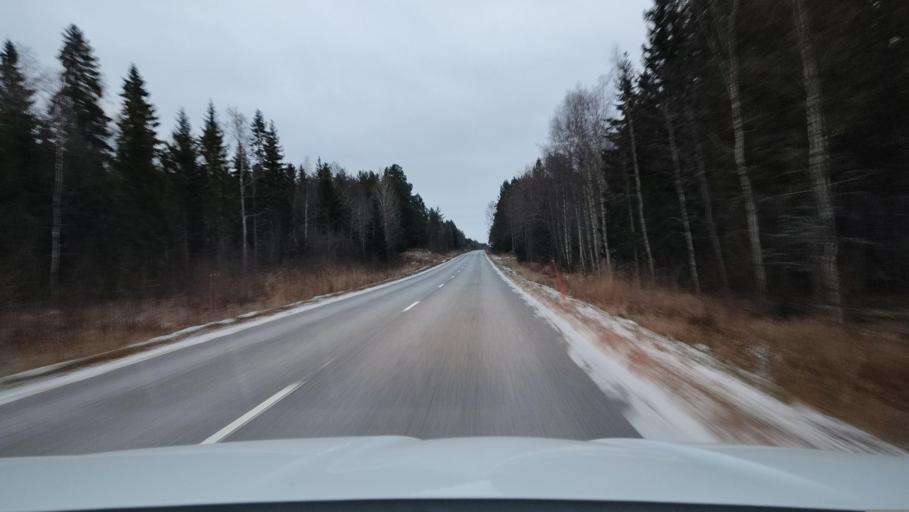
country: FI
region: Ostrobothnia
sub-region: Vaasa
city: Replot
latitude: 63.2527
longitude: 21.3716
